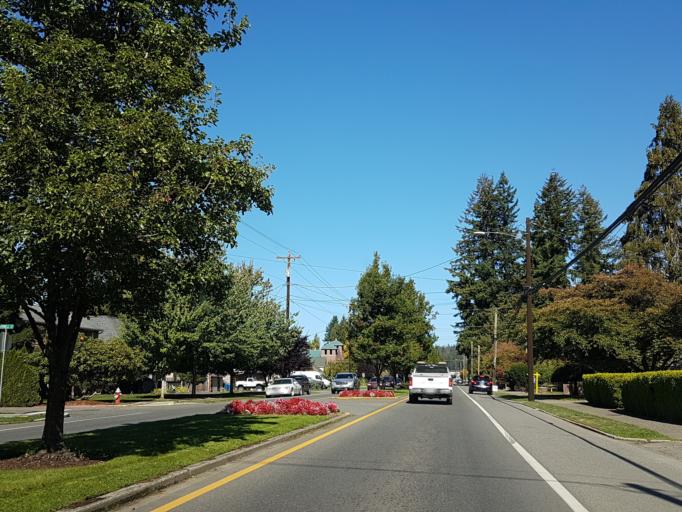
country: US
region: Washington
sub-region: Snohomish County
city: Monroe
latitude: 47.8502
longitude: -121.9707
